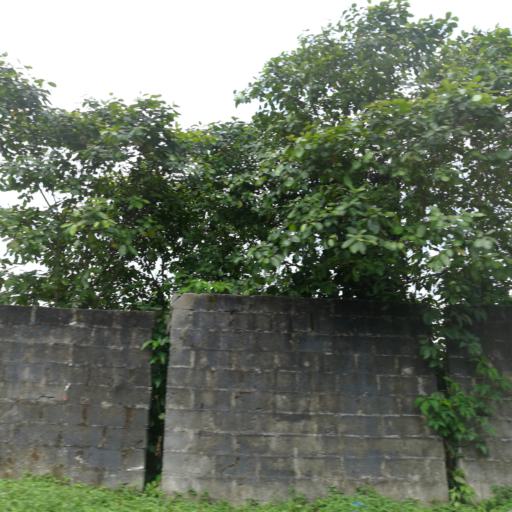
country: NG
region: Rivers
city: Port Harcourt
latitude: 4.8610
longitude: 7.0203
